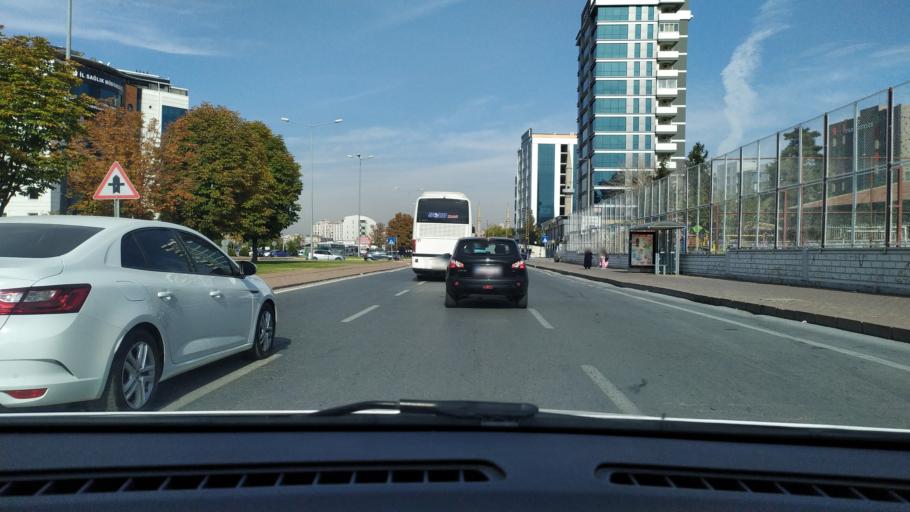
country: TR
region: Kayseri
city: Kayseri
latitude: 38.7116
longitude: 35.4911
